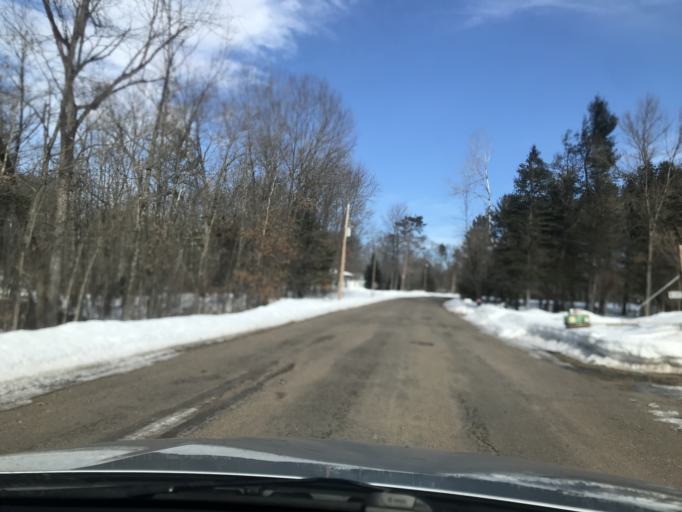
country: US
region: Wisconsin
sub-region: Oconto County
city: Gillett
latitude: 45.1201
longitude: -88.4191
